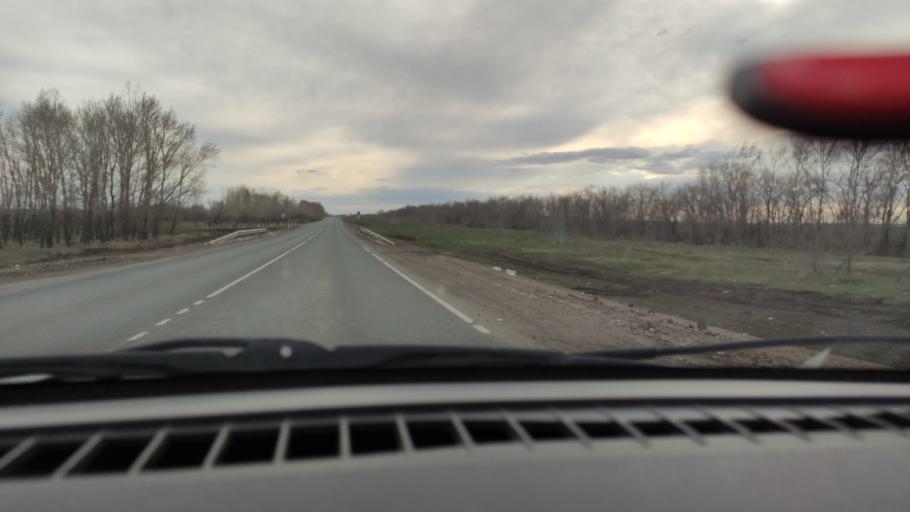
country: RU
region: Orenburg
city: Sakmara
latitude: 52.3267
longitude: 55.4936
